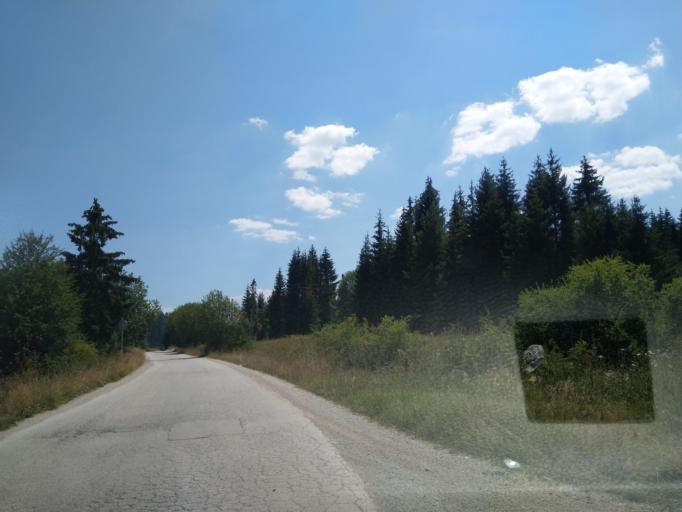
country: RS
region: Central Serbia
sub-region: Zlatiborski Okrug
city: Nova Varos
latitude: 43.4662
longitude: 19.9722
